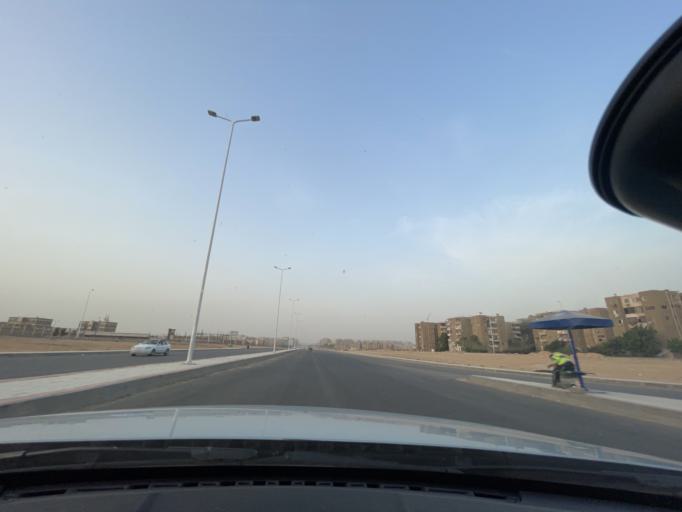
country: EG
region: Muhafazat al Qahirah
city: Cairo
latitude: 30.0381
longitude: 31.3569
